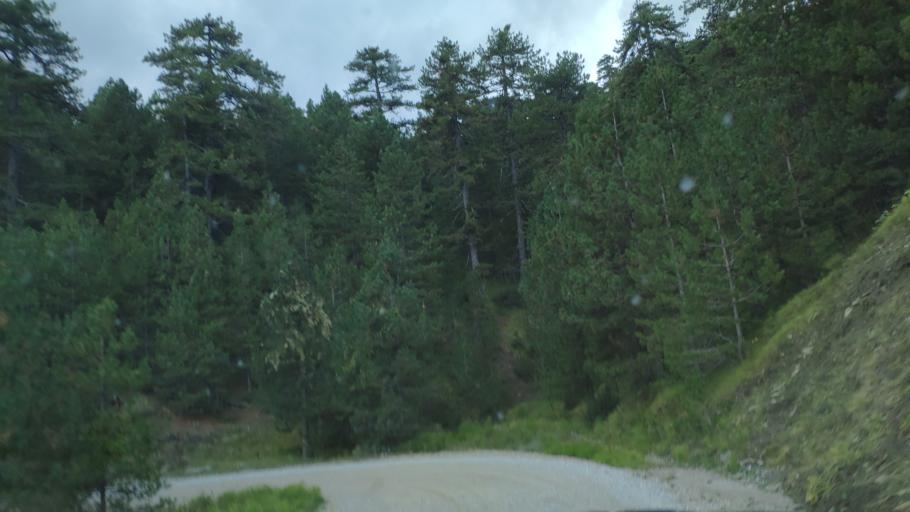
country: AL
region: Korce
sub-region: Rrethi i Kolonjes
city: Erseke
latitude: 40.2906
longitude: 20.8602
